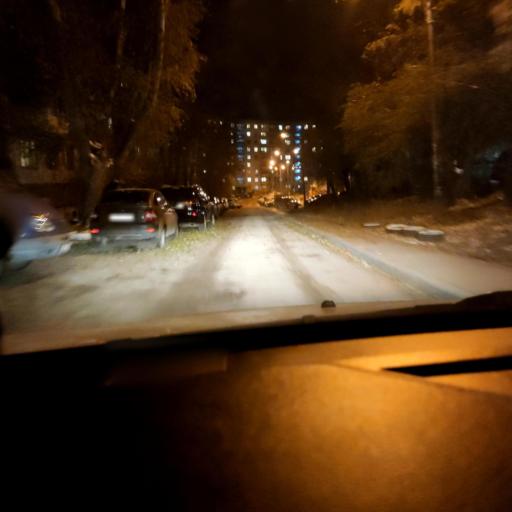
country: RU
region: Samara
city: Samara
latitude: 53.2449
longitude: 50.2184
